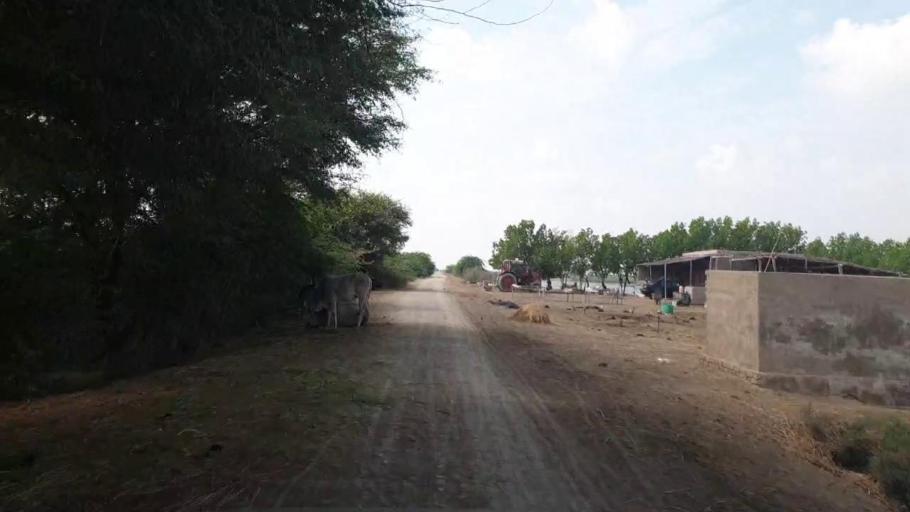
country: PK
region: Sindh
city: Badin
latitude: 24.5065
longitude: 68.6399
